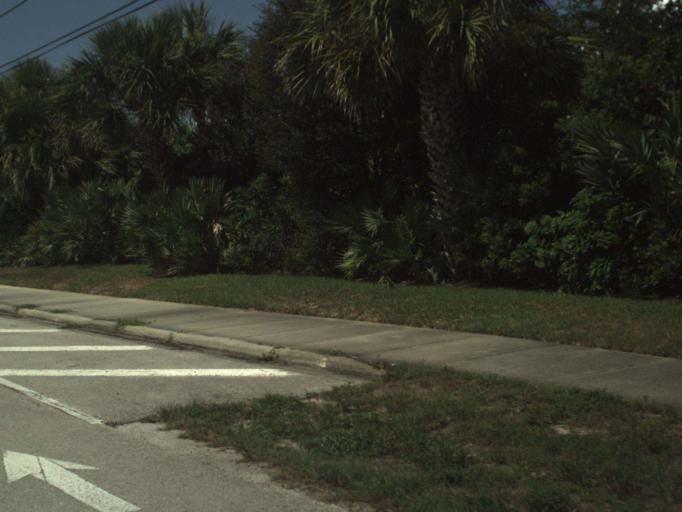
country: US
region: Florida
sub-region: Indian River County
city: Wabasso Beach
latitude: 27.7471
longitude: -80.3891
